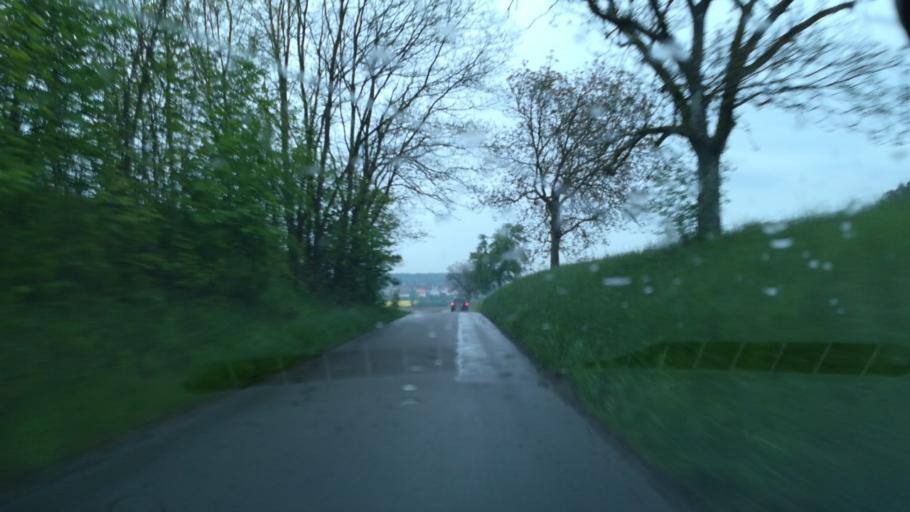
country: CH
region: Zurich
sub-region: Bezirk Buelach
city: End-Hoeri
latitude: 47.5188
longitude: 8.4980
